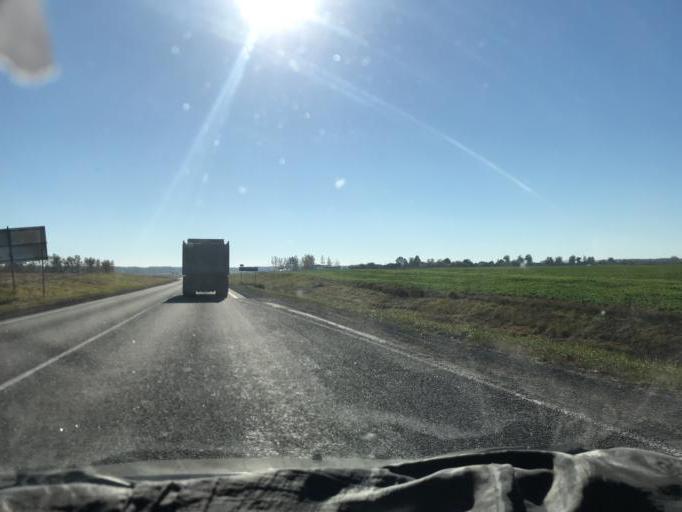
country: BY
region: Mogilev
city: Babruysk
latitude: 53.0752
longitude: 29.0713
